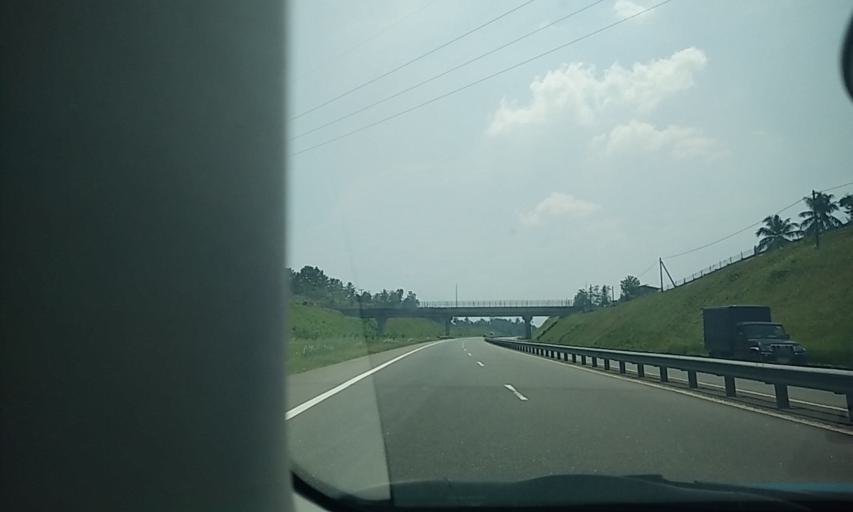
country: LK
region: Western
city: Horana South
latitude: 6.7506
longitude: 79.9960
